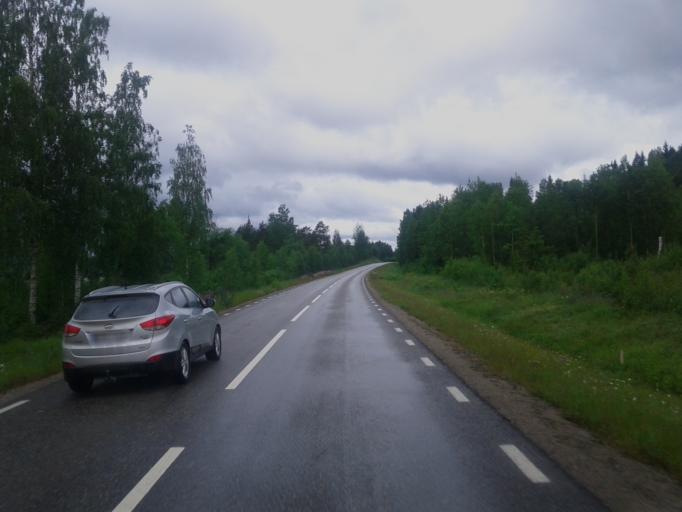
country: SE
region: Gaevleborg
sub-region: Nordanstigs Kommun
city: Bergsjoe
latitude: 62.0819
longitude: 16.8111
